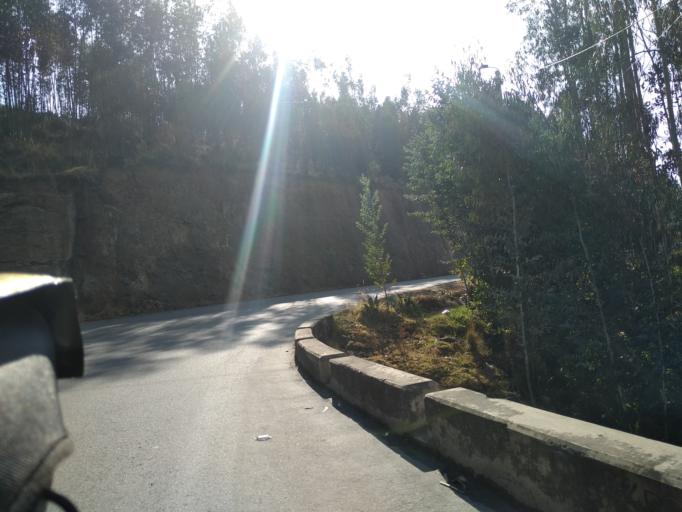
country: PE
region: La Libertad
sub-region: Provincia de Otuzco
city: Agallpampa
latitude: -7.9960
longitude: -78.5120
